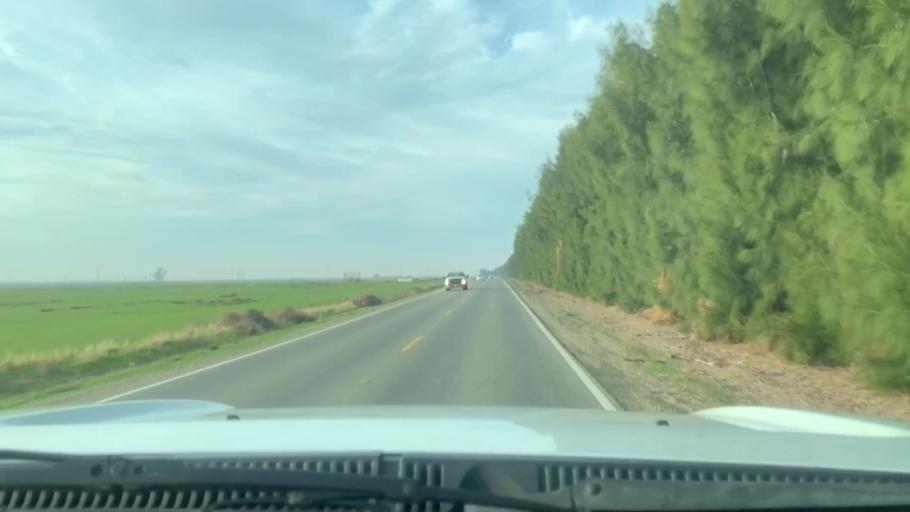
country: US
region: California
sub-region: Kern County
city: Lost Hills
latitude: 35.5186
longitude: -119.7538
